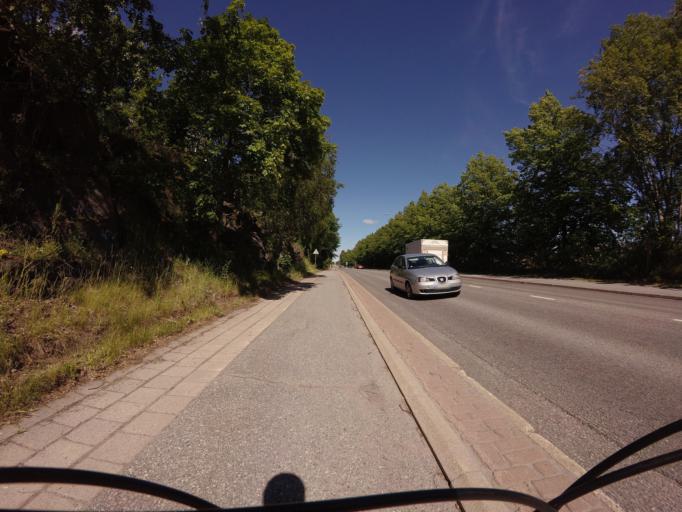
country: FI
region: Varsinais-Suomi
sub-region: Turku
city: Turku
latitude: 60.4567
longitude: 22.2520
